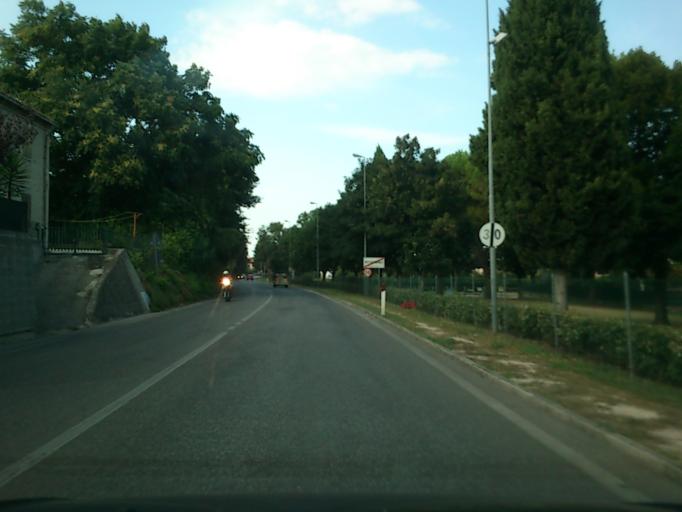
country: IT
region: The Marches
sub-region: Provincia di Pesaro e Urbino
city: Rosciano
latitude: 43.8194
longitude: 12.9917
